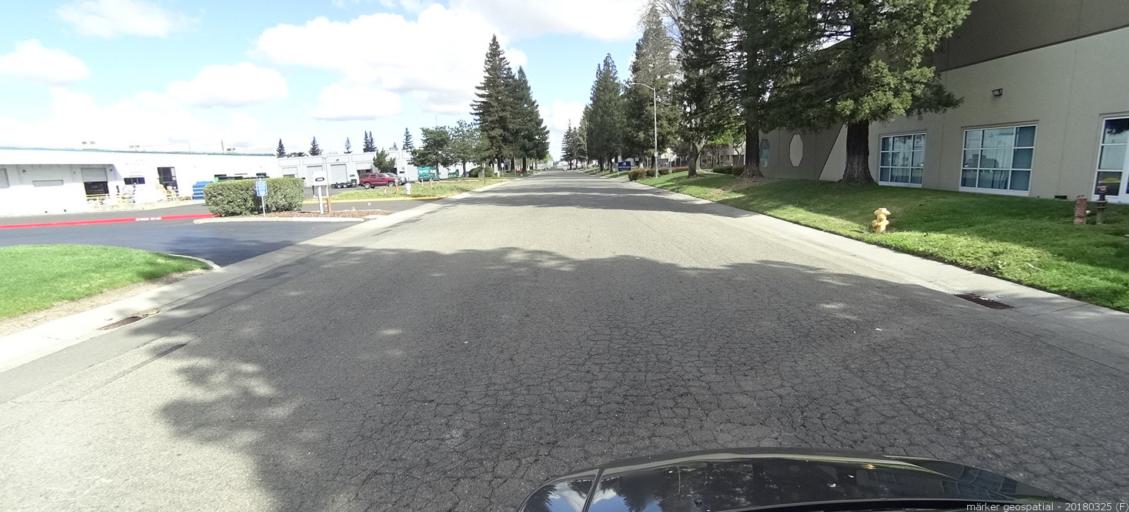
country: US
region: California
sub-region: Sacramento County
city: Rio Linda
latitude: 38.6447
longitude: -121.4818
